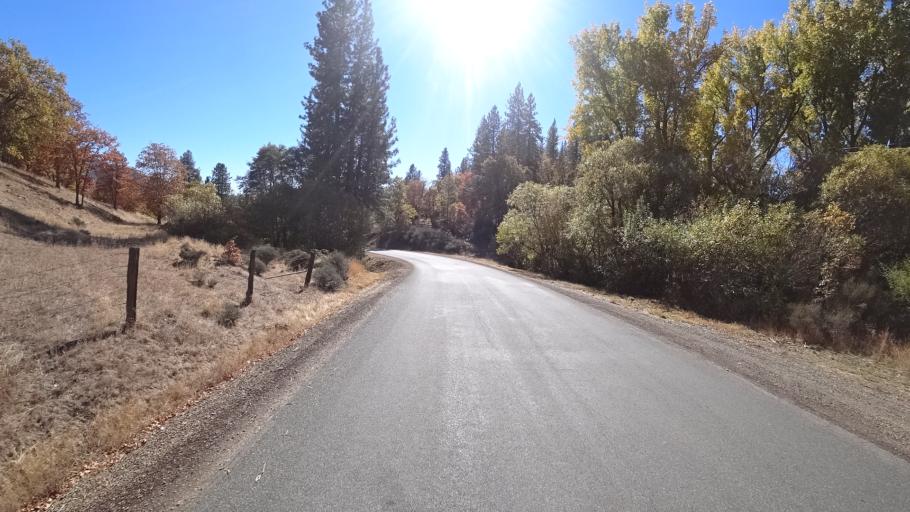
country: US
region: California
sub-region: Siskiyou County
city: Yreka
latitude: 41.6080
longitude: -122.9787
